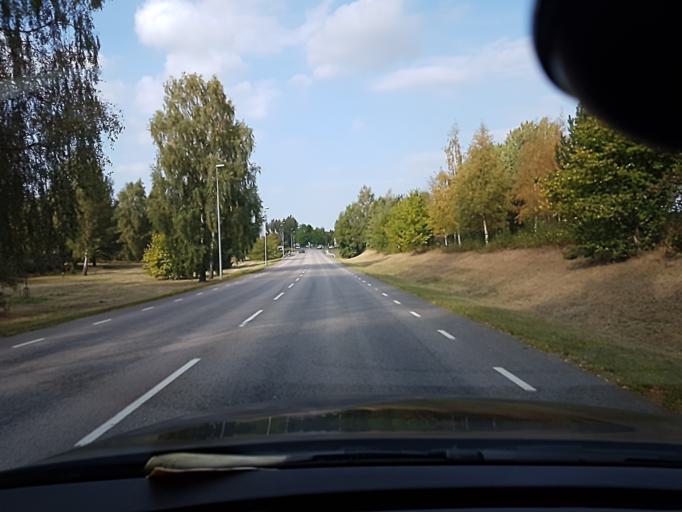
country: SE
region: Kronoberg
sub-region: Vaxjo Kommun
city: Vaexjoe
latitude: 56.8481
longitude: 14.8239
